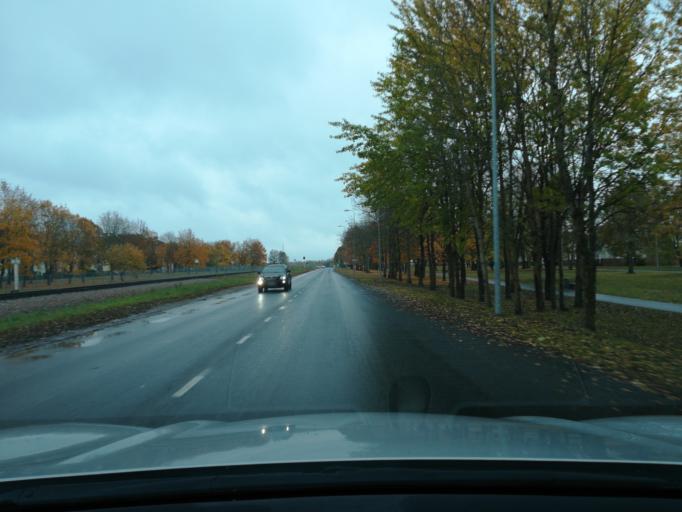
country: EE
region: Ida-Virumaa
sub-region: Johvi vald
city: Johvi
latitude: 59.3238
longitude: 27.4221
